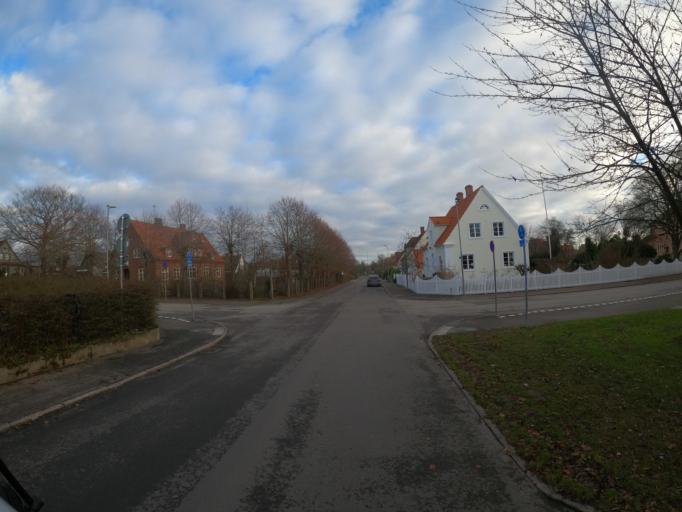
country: SE
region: Skane
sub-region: Svedala Kommun
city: Svedala
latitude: 55.5120
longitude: 13.2370
